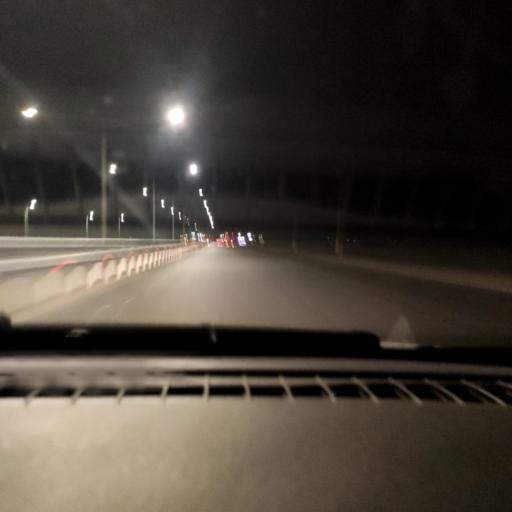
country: RU
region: Lipetsk
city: Khlevnoye
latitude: 52.0446
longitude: 39.1967
